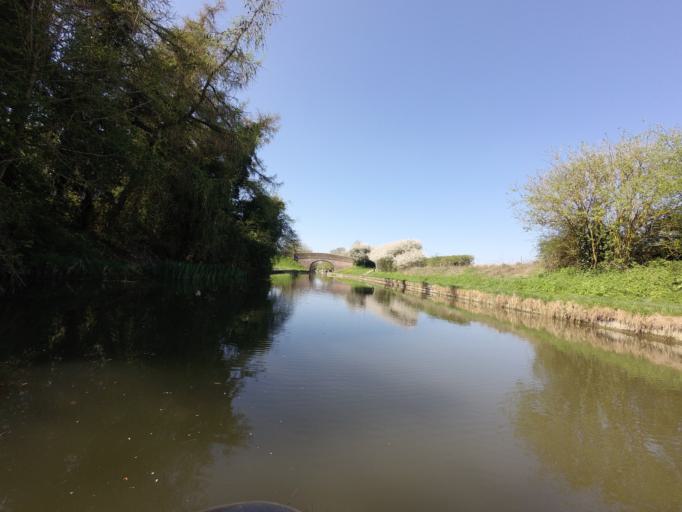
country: GB
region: England
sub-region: Hertfordshire
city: Tring
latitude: 51.7892
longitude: -0.6174
